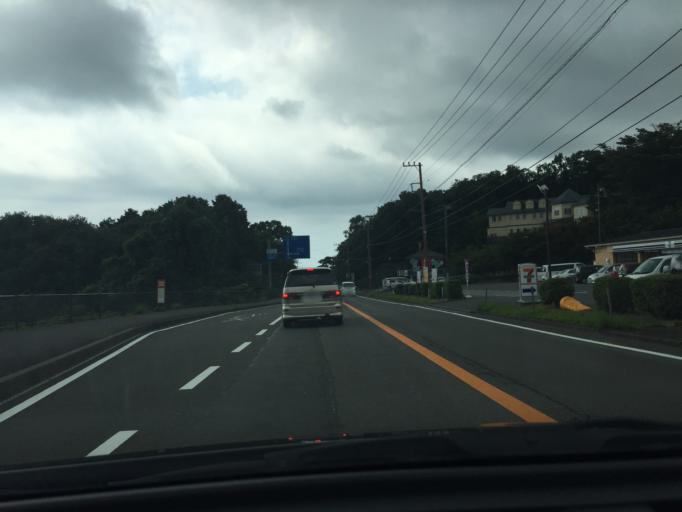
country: JP
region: Shizuoka
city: Ito
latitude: 34.9118
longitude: 139.1199
